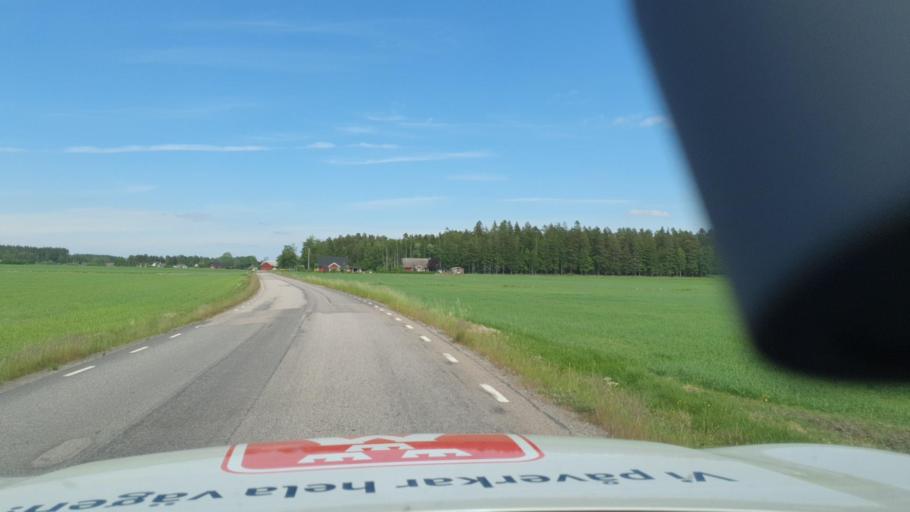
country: SE
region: Vaestra Goetaland
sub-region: Essunga Kommun
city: Nossebro
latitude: 58.2244
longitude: 12.6510
